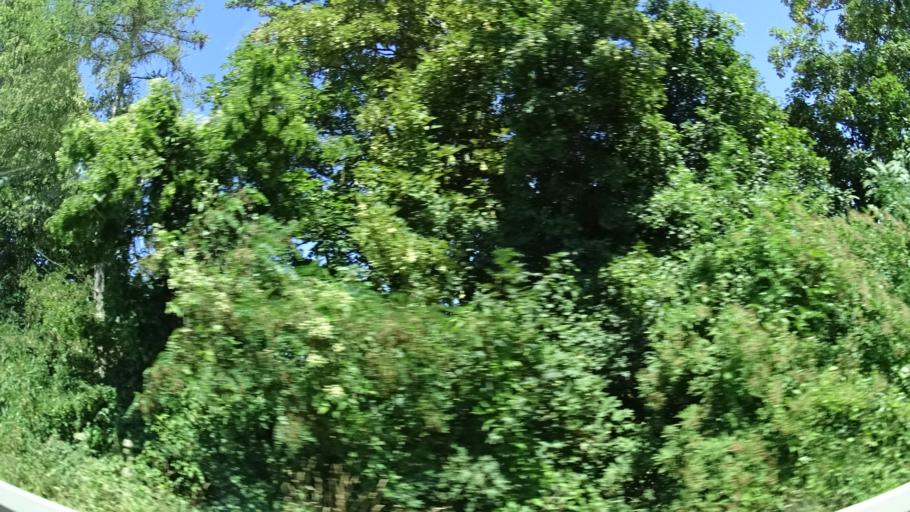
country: DE
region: Bavaria
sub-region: Regierungsbezirk Unterfranken
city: Guntersleben
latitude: 49.8681
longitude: 9.9243
